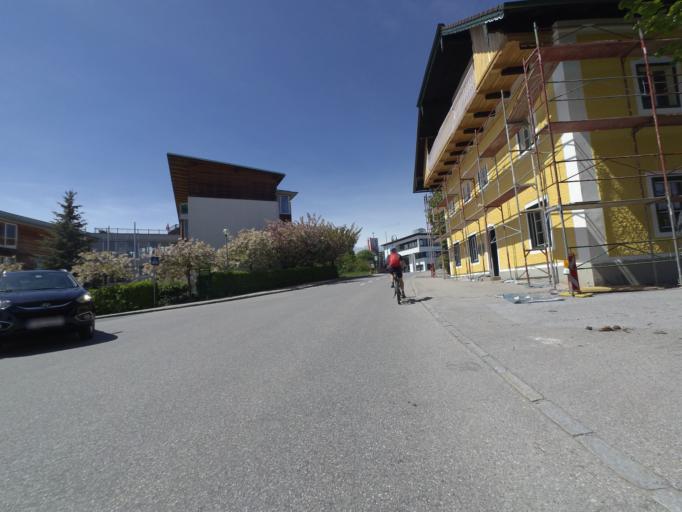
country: AT
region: Salzburg
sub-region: Politischer Bezirk Salzburg-Umgebung
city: Obertrum am See
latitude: 47.9376
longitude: 13.0743
